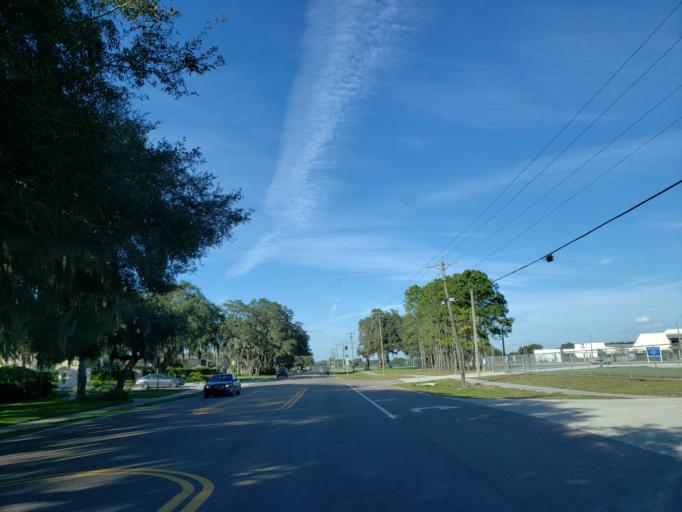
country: US
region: Florida
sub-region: Hillsborough County
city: Riverview
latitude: 27.8487
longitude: -82.3145
